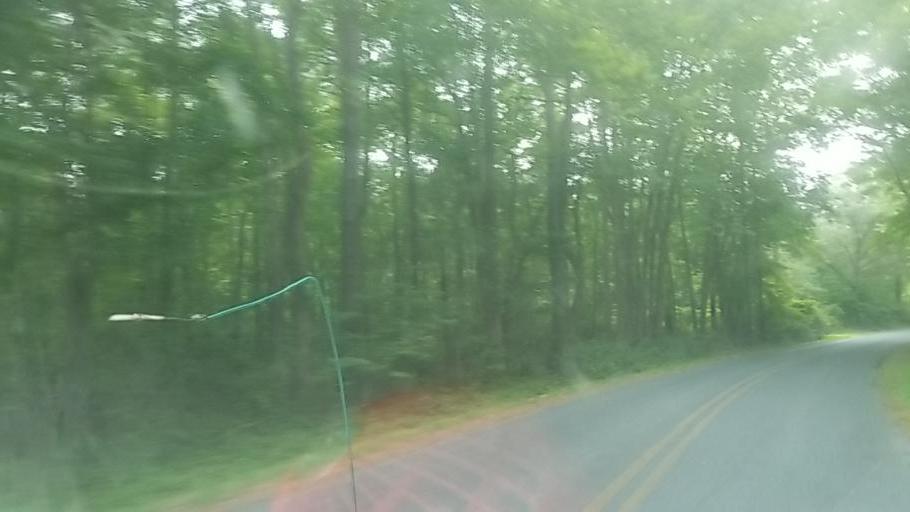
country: US
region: Maryland
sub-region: Wicomico County
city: Pittsville
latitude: 38.4151
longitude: -75.4798
